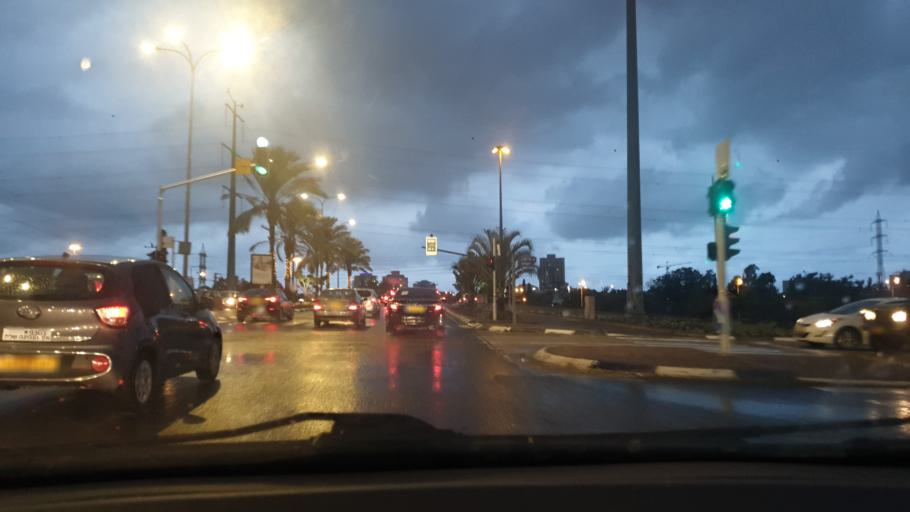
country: IL
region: Central District
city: Rishon LeZiyyon
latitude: 31.9770
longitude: 34.7942
